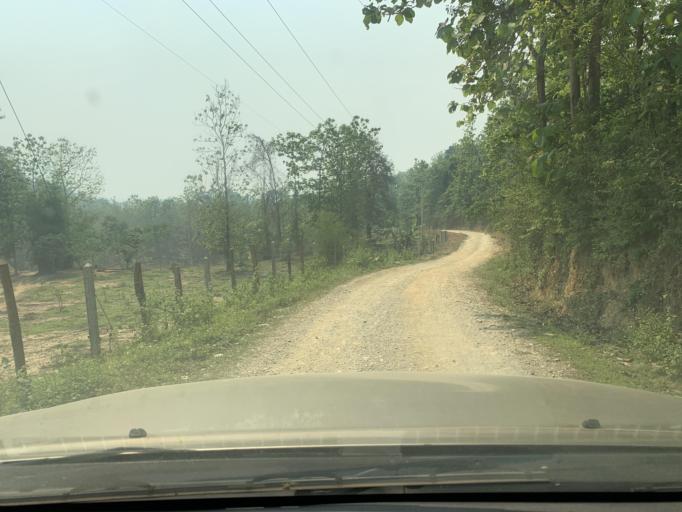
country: LA
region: Louangphabang
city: Louangphabang
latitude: 19.8836
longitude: 102.2558
